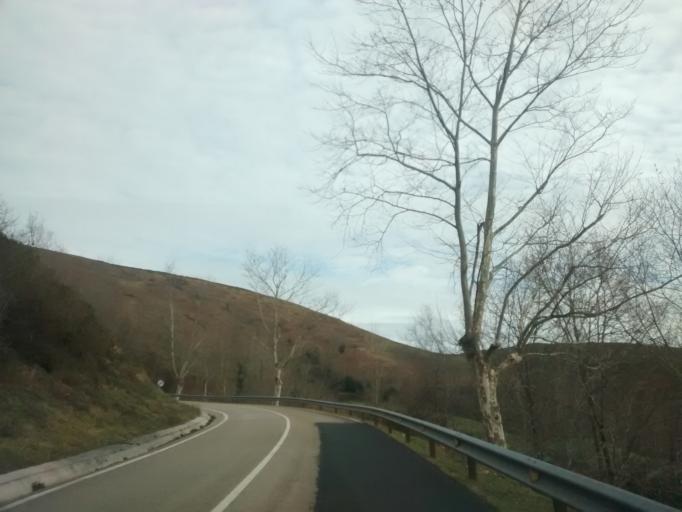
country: ES
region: Cantabria
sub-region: Provincia de Cantabria
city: Ruente
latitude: 43.2472
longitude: -4.3280
